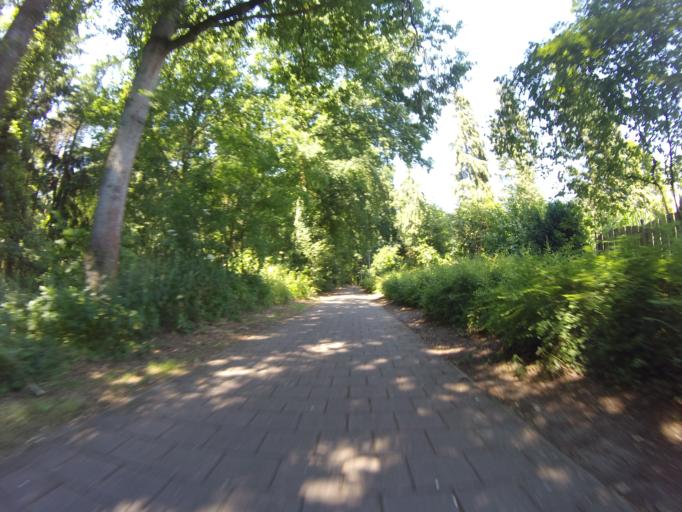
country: NL
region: Drenthe
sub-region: Gemeente Emmen
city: Emmen
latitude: 52.7863
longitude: 6.9307
